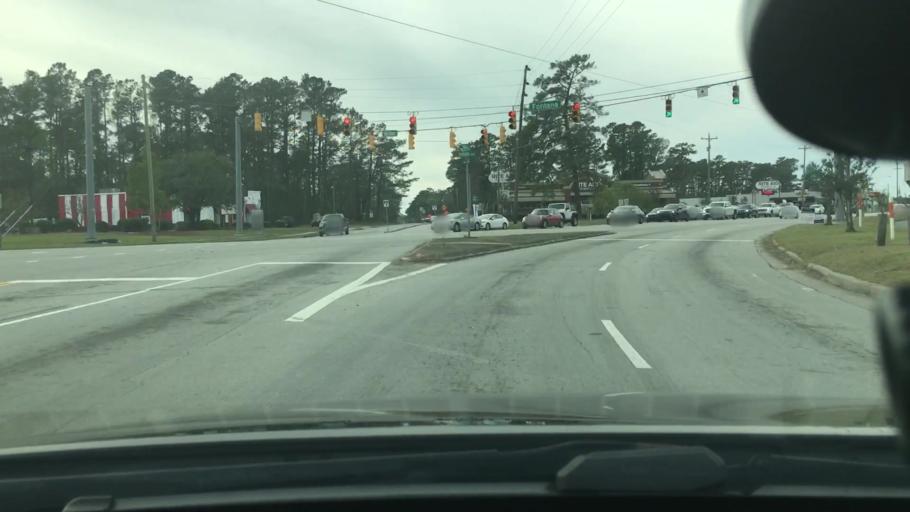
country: US
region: North Carolina
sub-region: Craven County
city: Havelock
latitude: 34.8828
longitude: -76.9096
